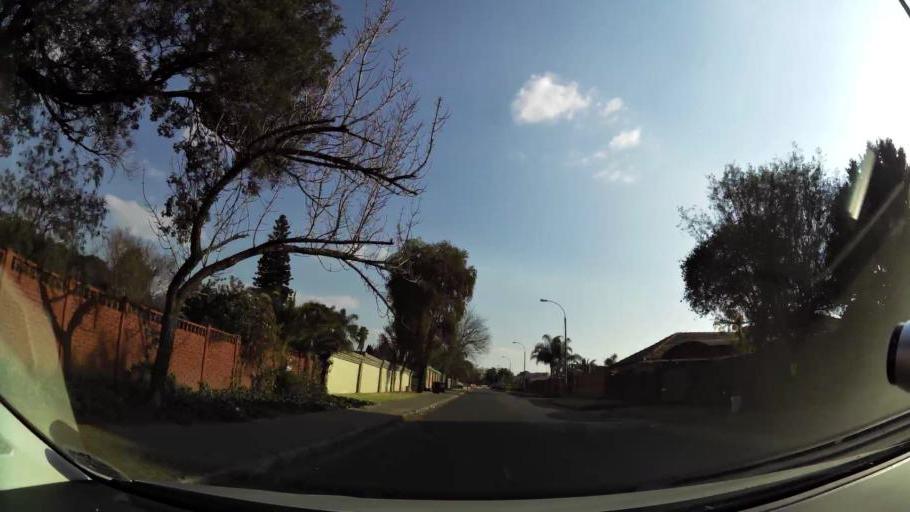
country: ZA
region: Gauteng
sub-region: City of Johannesburg Metropolitan Municipality
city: Modderfontein
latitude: -26.0769
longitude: 28.2084
